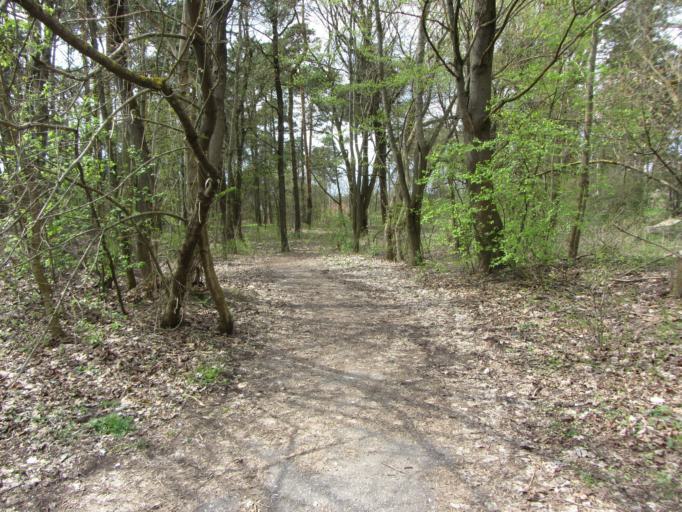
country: LT
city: Lentvaris
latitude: 54.6488
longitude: 25.0563
